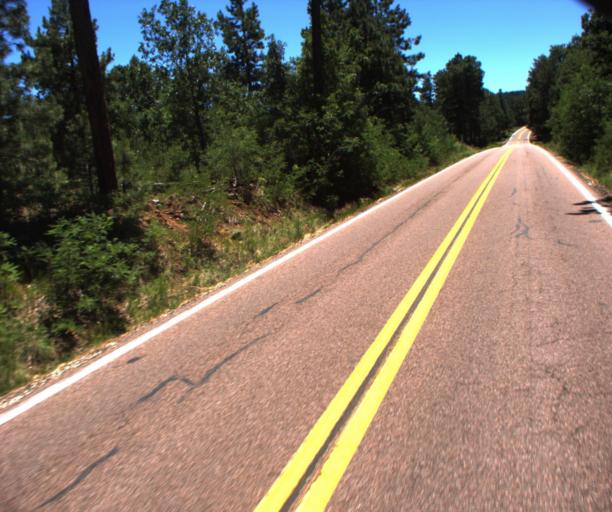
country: US
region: Arizona
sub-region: Gila County
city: Pine
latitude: 34.4771
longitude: -111.3812
